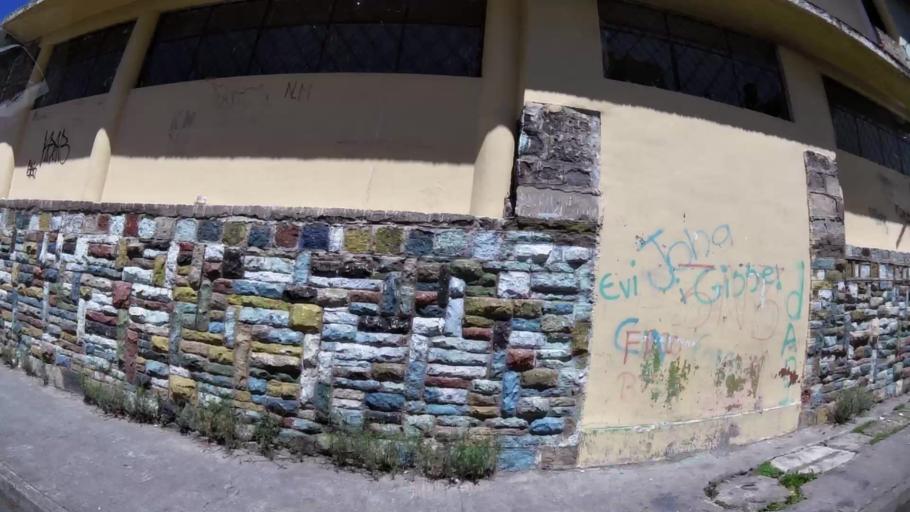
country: EC
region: Chimborazo
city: Riobamba
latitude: -1.6767
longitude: -78.6502
